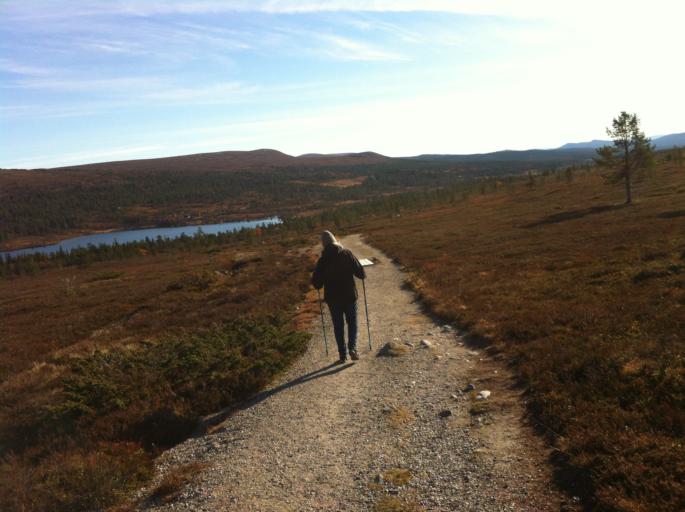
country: NO
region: Hedmark
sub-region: Engerdal
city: Engerdal
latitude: 62.1125
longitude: 12.2726
